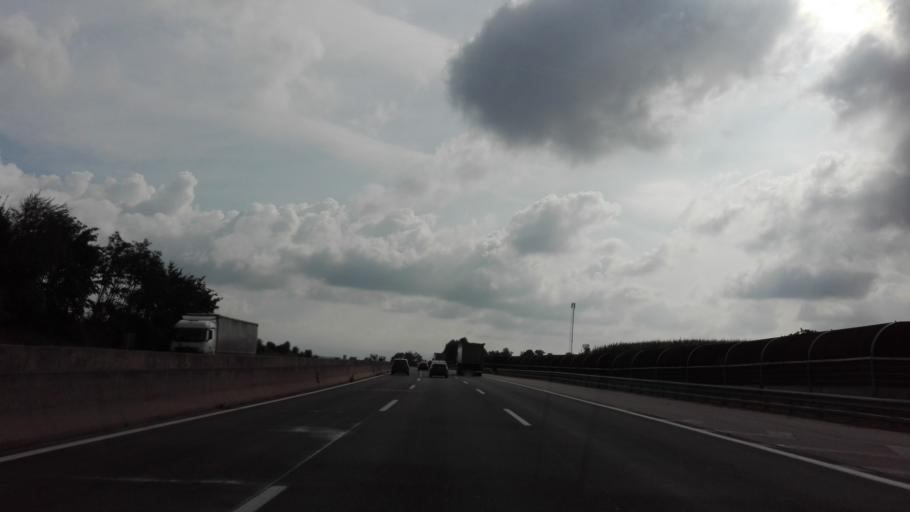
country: AT
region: Lower Austria
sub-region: Politischer Bezirk Amstetten
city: Strengberg
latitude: 48.1160
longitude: 14.6349
